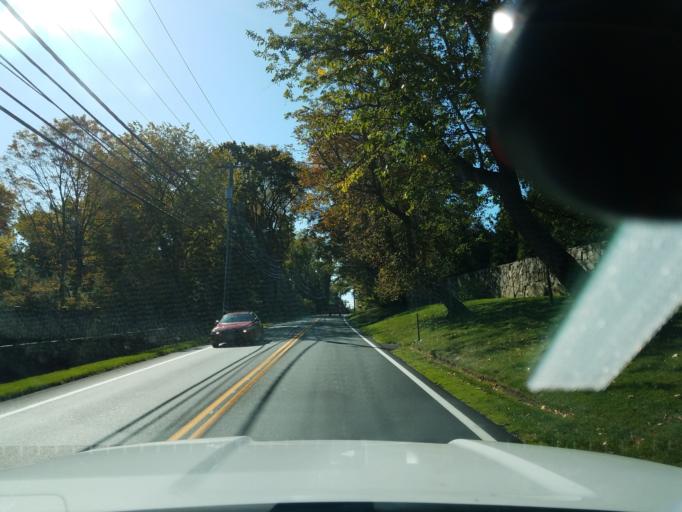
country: US
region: Connecticut
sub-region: Fairfield County
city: Cos Cob
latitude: 41.0787
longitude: -73.6239
